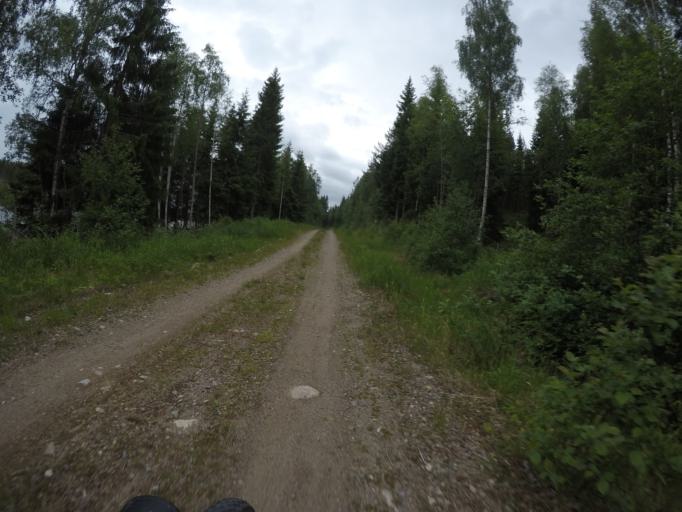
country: SE
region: Dalarna
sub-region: Ludvika Kommun
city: Abborrberget
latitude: 60.0445
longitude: 14.5920
